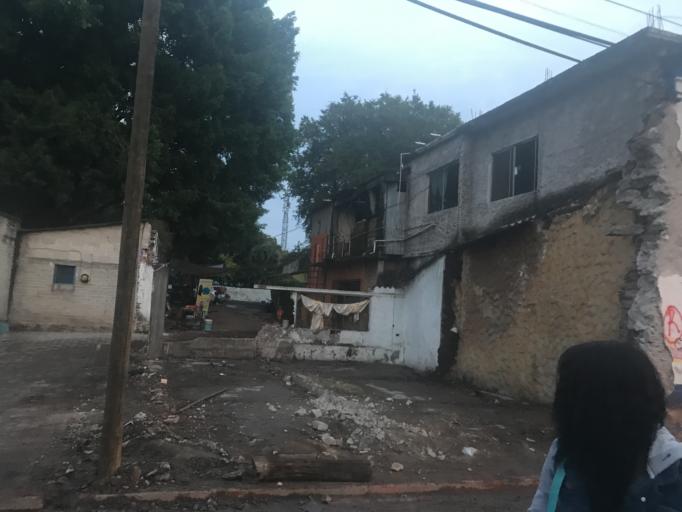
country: MX
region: Morelos
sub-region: Jojutla
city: Jojutla
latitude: 18.6123
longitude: -99.1803
